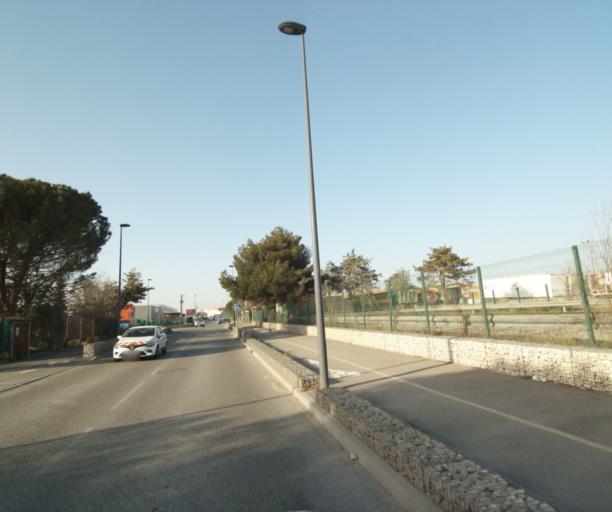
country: FR
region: Provence-Alpes-Cote d'Azur
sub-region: Departement des Bouches-du-Rhone
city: Saint-Victoret
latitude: 43.4278
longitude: 5.2498
